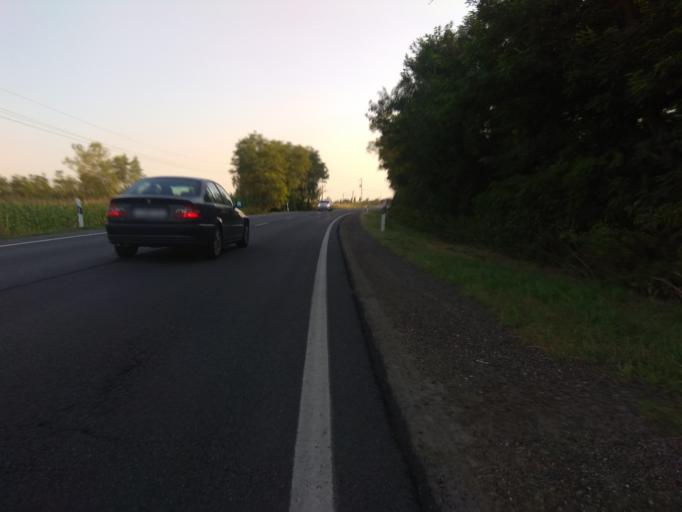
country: HU
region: Borsod-Abauj-Zemplen
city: Emod
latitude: 47.9483
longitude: 20.8324
